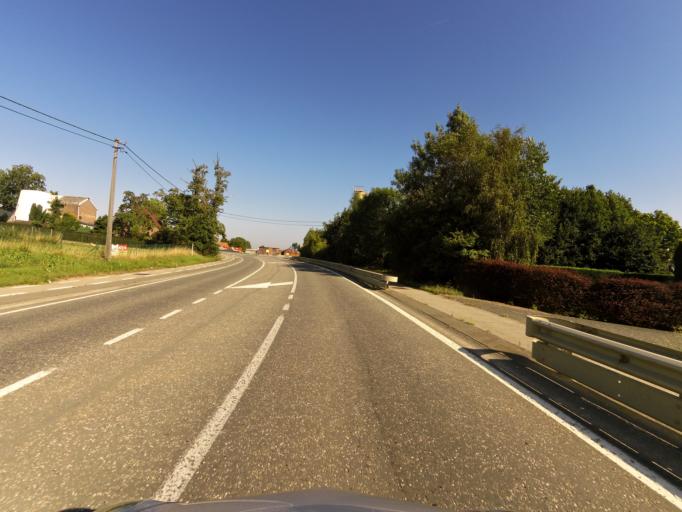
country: BE
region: Wallonia
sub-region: Province du Hainaut
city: Flobecq
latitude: 50.8120
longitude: 3.7363
